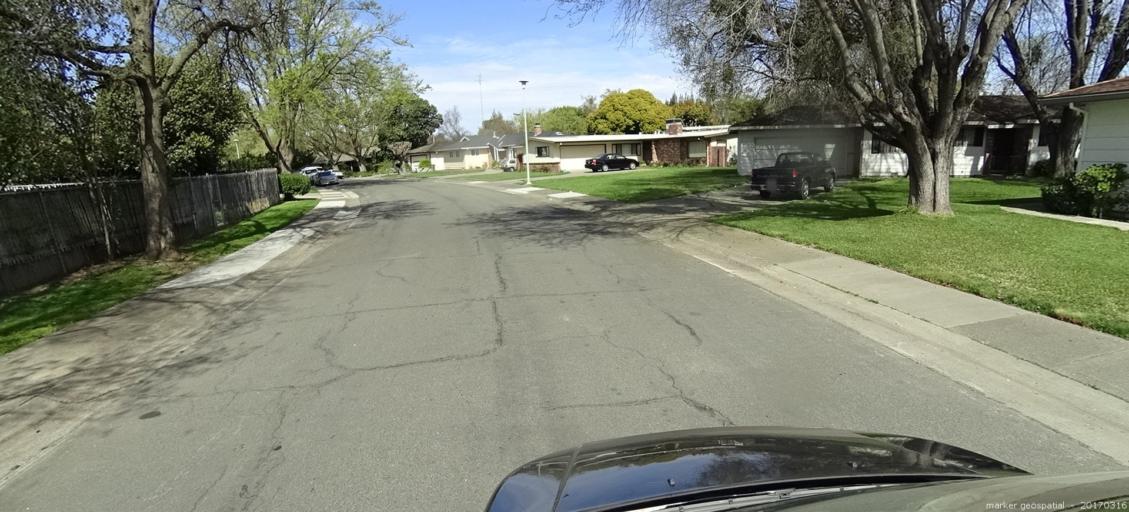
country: US
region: California
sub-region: Sacramento County
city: Parkway
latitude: 38.4975
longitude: -121.5028
